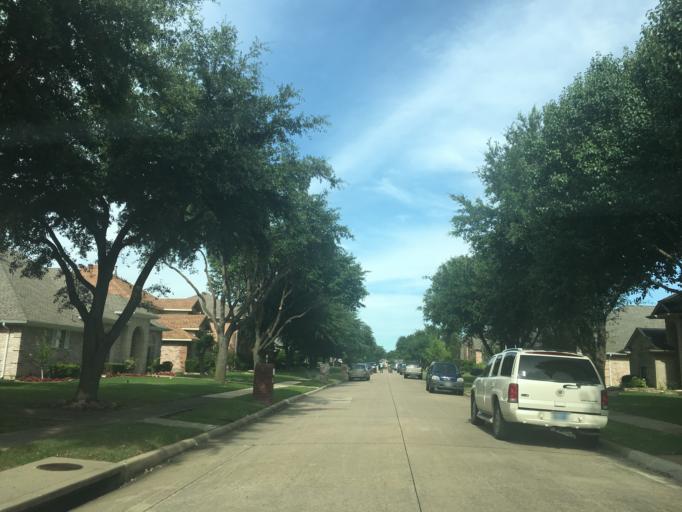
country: US
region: Texas
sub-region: Dallas County
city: Richardson
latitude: 32.9344
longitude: -96.7169
